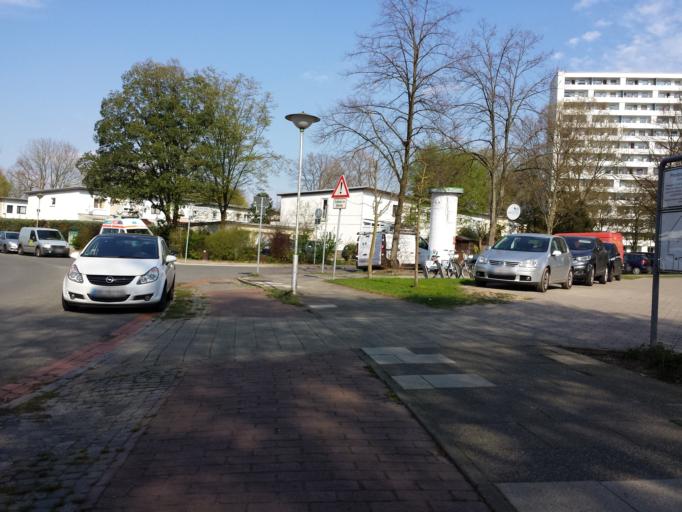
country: DE
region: Lower Saxony
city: Lilienthal
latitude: 53.0833
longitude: 8.8993
